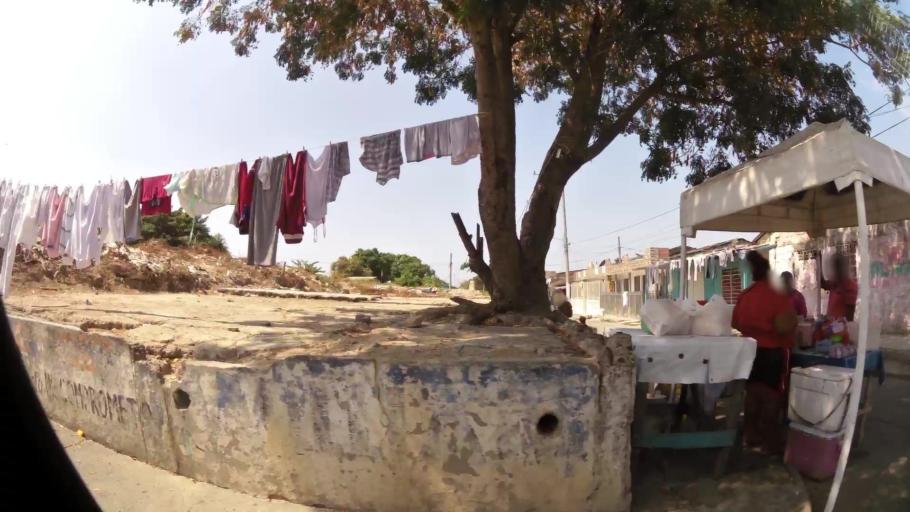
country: CO
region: Bolivar
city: Cartagena
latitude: 10.4038
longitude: -75.4895
